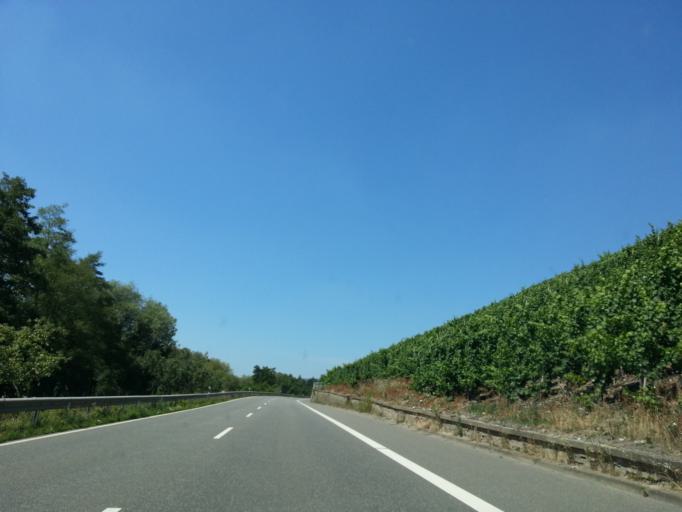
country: DE
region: Rheinland-Pfalz
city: Mehring
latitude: 49.7965
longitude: 6.8096
